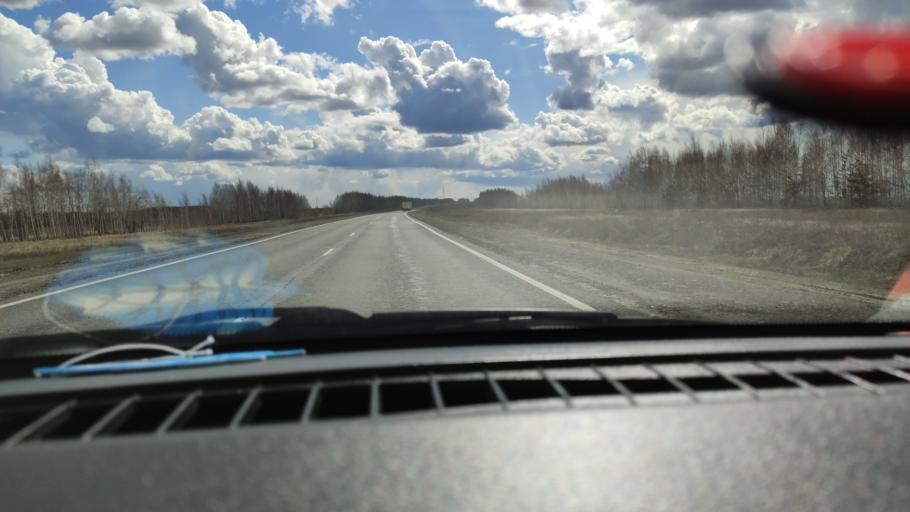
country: RU
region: Saratov
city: Dukhovnitskoye
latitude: 52.8474
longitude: 48.2539
